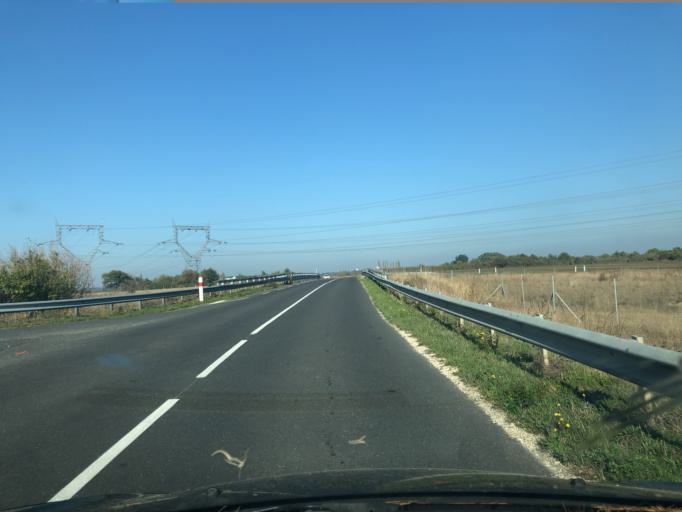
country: FR
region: Centre
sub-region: Departement d'Indre-et-Loire
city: Rouziers-de-Touraine
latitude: 47.4946
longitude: 0.6552
